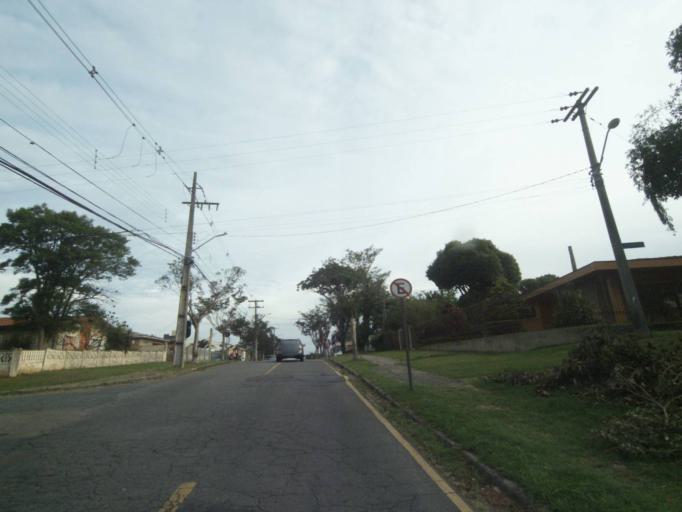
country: BR
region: Parana
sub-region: Curitiba
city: Curitiba
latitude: -25.4309
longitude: -49.2364
